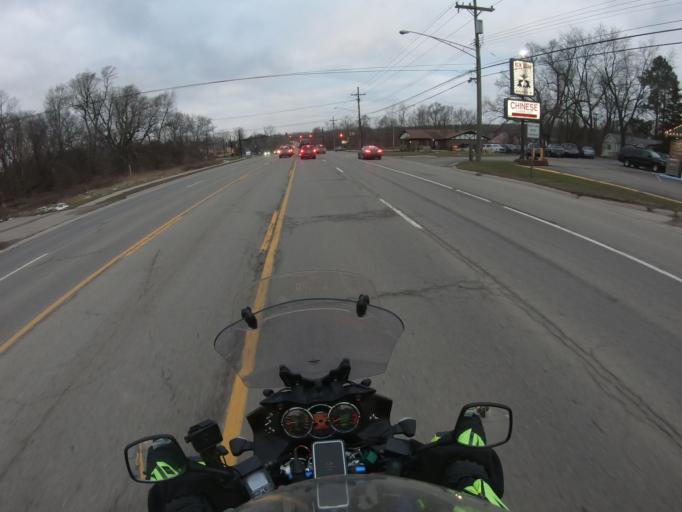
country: US
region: Michigan
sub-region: Oakland County
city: Clarkston
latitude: 42.7583
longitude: -83.4816
